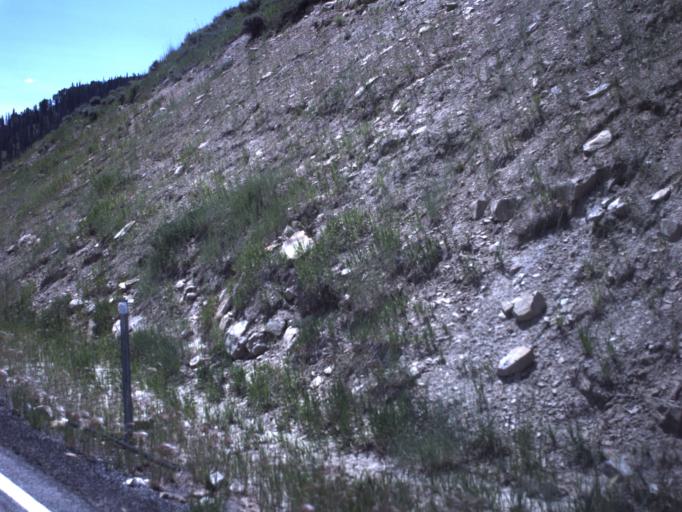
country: US
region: Utah
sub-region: Sanpete County
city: Fairview
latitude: 39.6805
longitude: -111.2432
